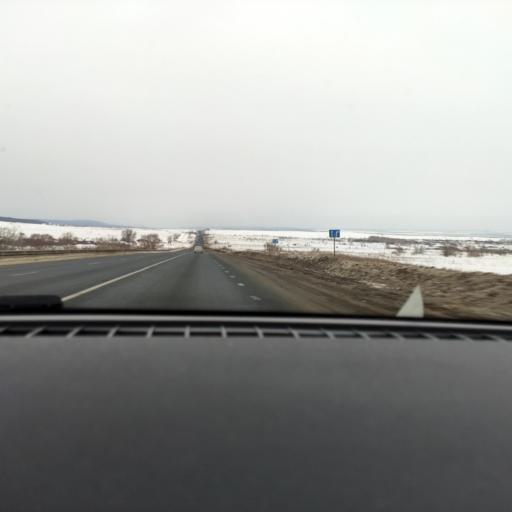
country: RU
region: Samara
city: Novosemeykino
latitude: 53.3996
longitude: 50.4147
